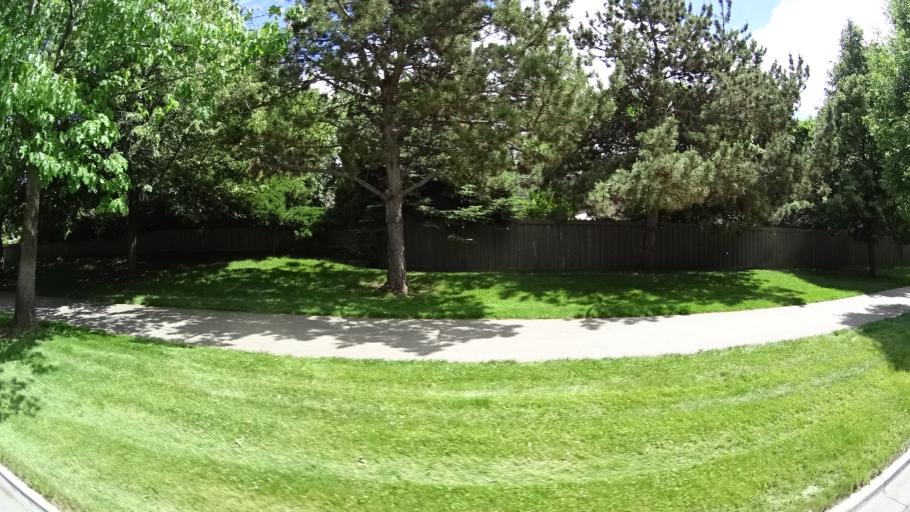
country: US
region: Idaho
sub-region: Ada County
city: Boise
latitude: 43.5780
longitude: -116.1585
